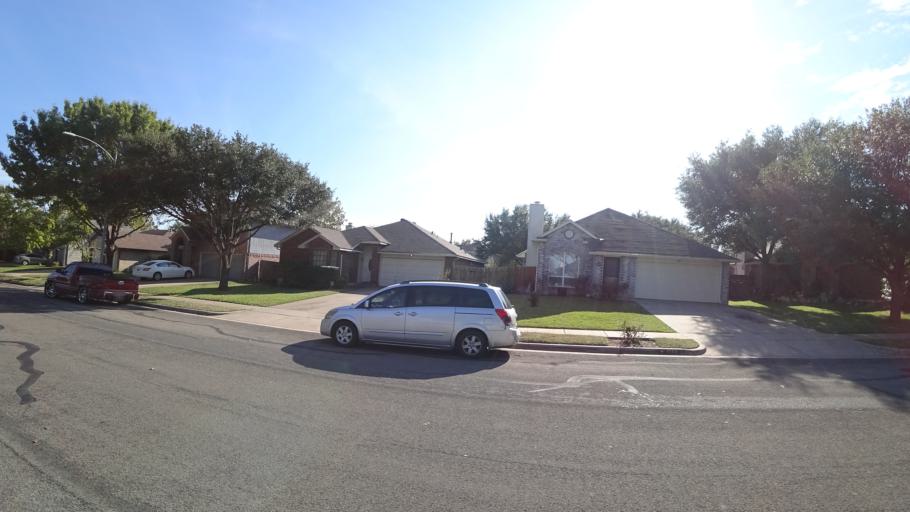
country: US
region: Texas
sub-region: Travis County
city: Pflugerville
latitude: 30.4070
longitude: -97.6473
